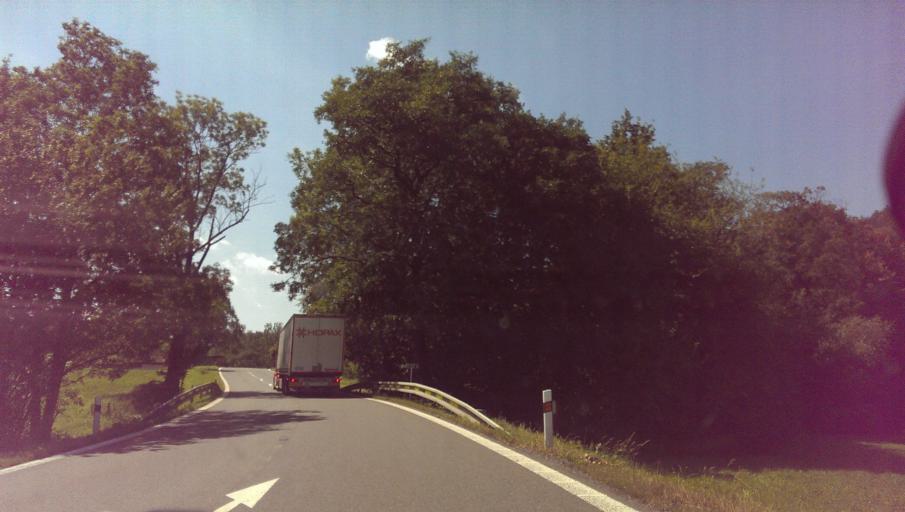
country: CZ
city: Lichnov (o. Novy Jicin)
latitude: 49.5757
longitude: 18.1837
